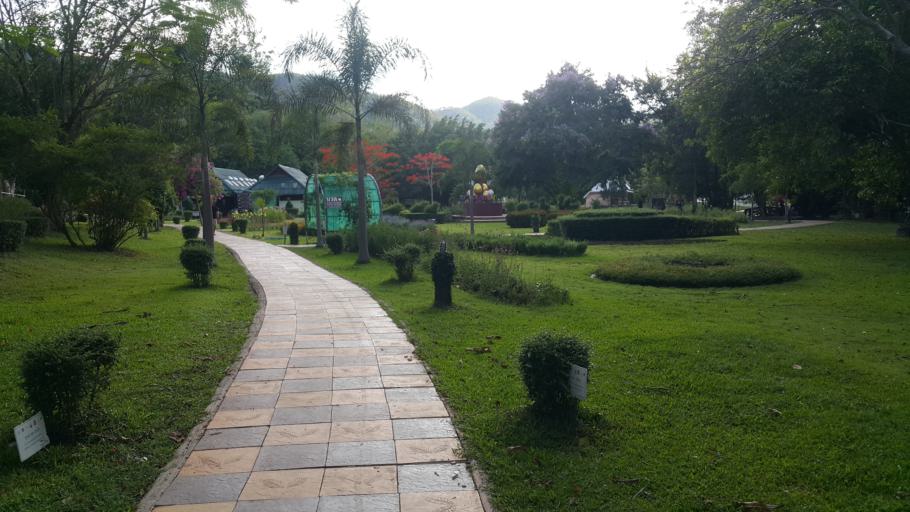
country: TH
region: Chiang Mai
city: Mae On
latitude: 18.8151
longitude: 99.2289
